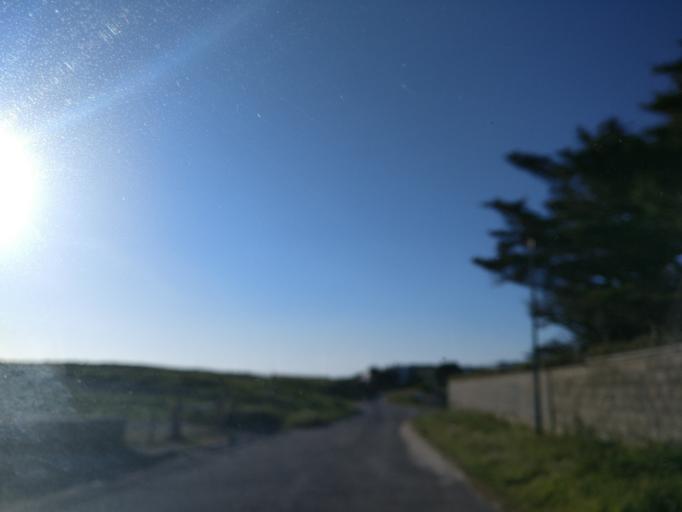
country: FR
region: Brittany
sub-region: Departement du Finistere
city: Porspoder
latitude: 48.5194
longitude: -4.7625
